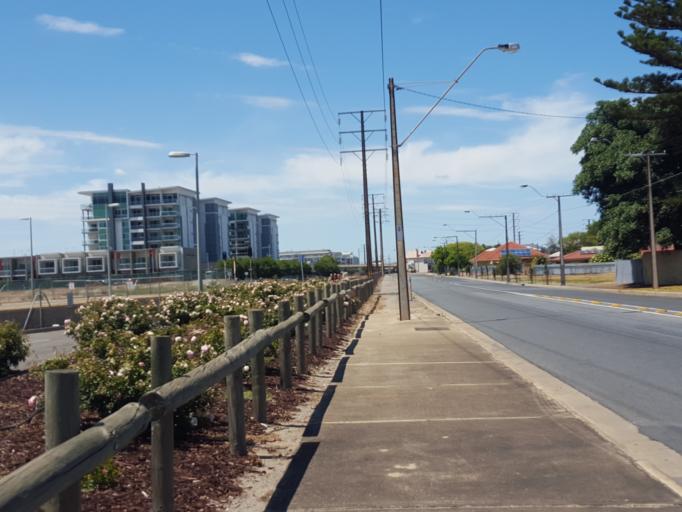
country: AU
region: South Australia
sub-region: Port Adelaide Enfield
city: Birkenhead
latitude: -34.8424
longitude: 138.4931
